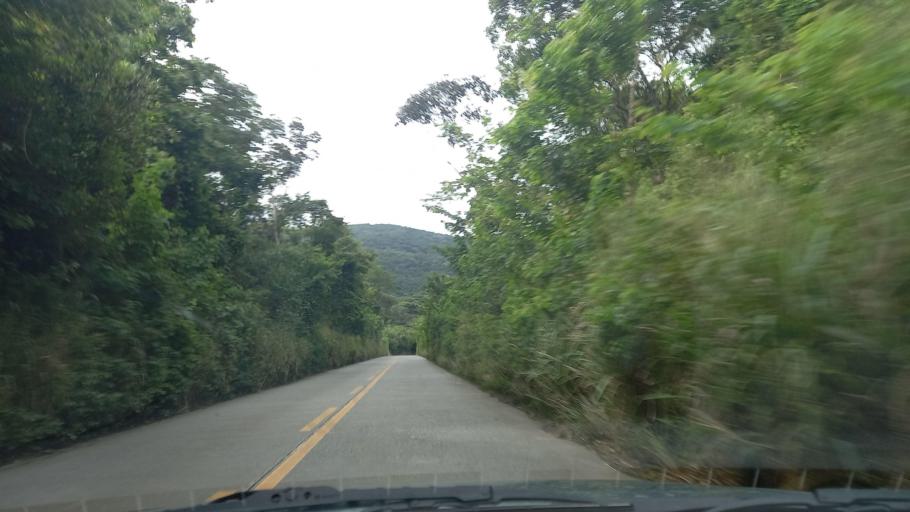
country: BR
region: Pernambuco
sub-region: Maraial
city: Maraial
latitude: -8.7717
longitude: -35.8667
